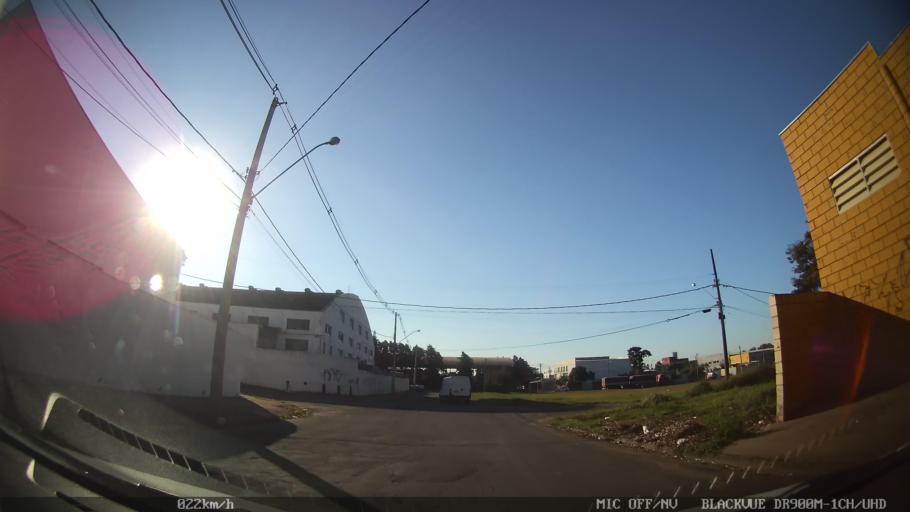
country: BR
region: Sao Paulo
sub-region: Nova Odessa
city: Nova Odessa
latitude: -22.7761
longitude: -47.2894
